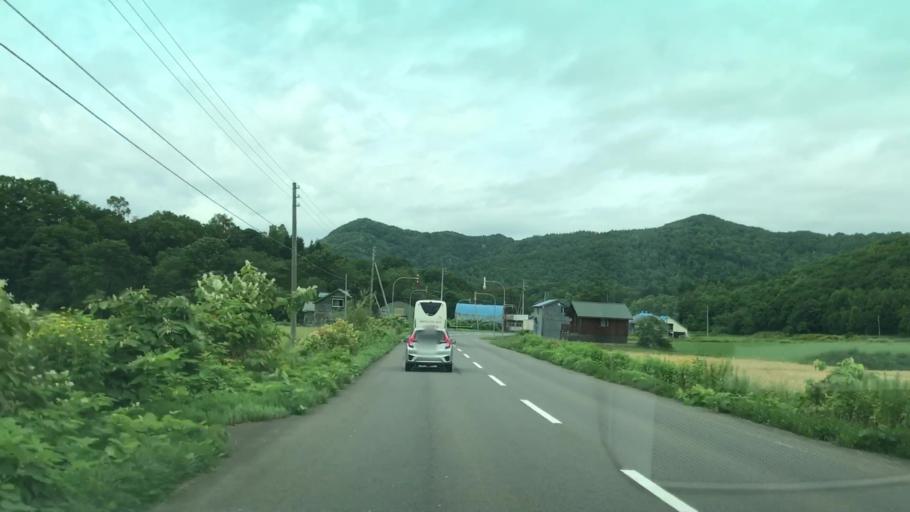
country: JP
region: Hokkaido
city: Niseko Town
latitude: 42.9476
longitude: 140.8345
